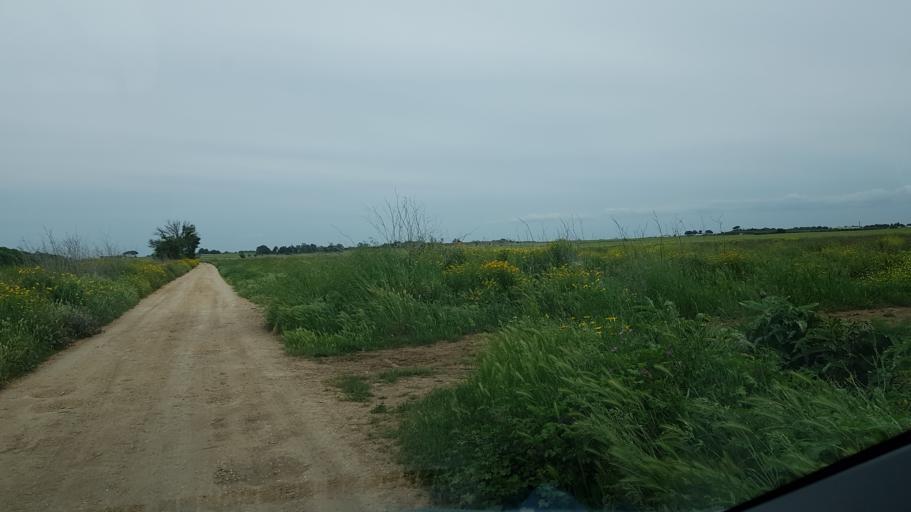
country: IT
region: Apulia
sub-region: Provincia di Brindisi
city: Brindisi
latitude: 40.6601
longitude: 17.8803
